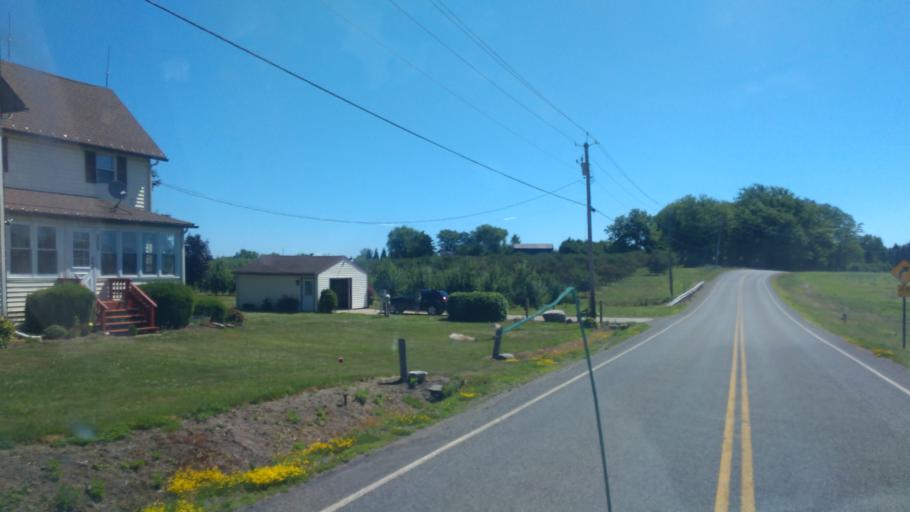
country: US
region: New York
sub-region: Wayne County
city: Sodus
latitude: 43.2713
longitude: -77.0828
